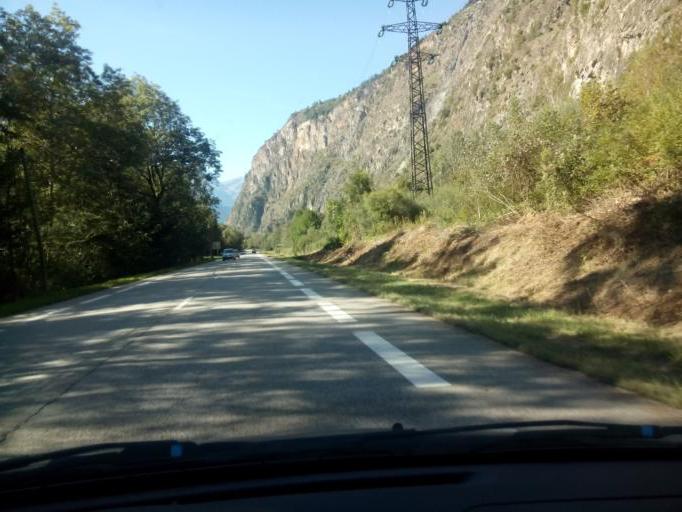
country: FR
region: Rhone-Alpes
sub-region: Departement de l'Isere
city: Huez
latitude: 45.0410
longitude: 6.0606
